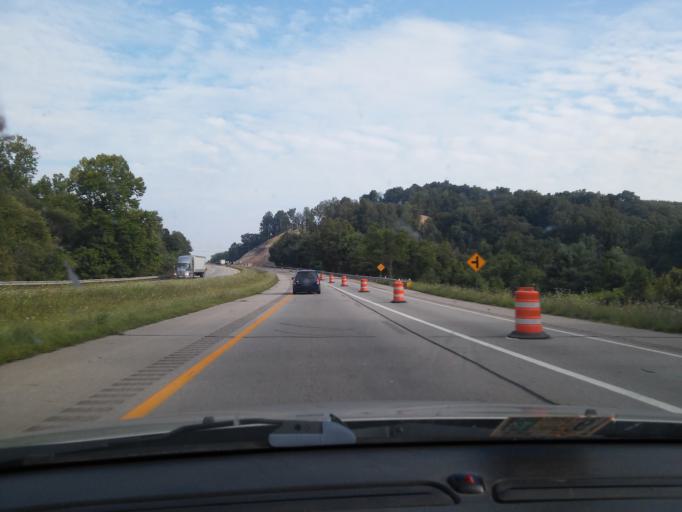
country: US
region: Ohio
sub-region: Jackson County
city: Jackson
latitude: 39.1123
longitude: -82.6802
